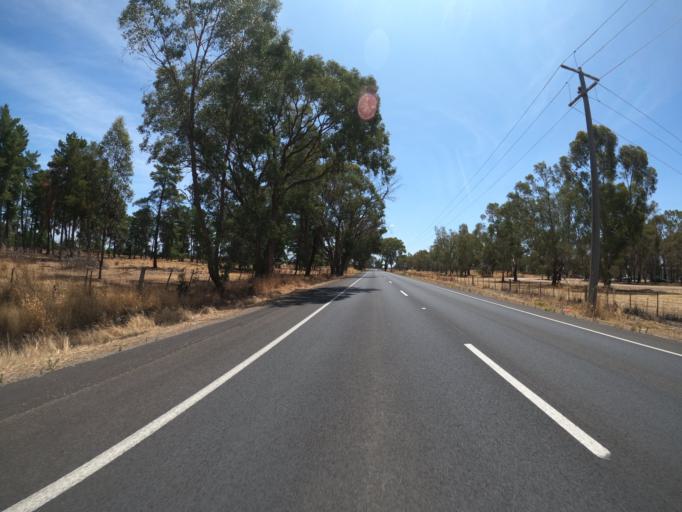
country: AU
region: Victoria
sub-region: Benalla
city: Benalla
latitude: -36.5261
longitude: 146.0384
